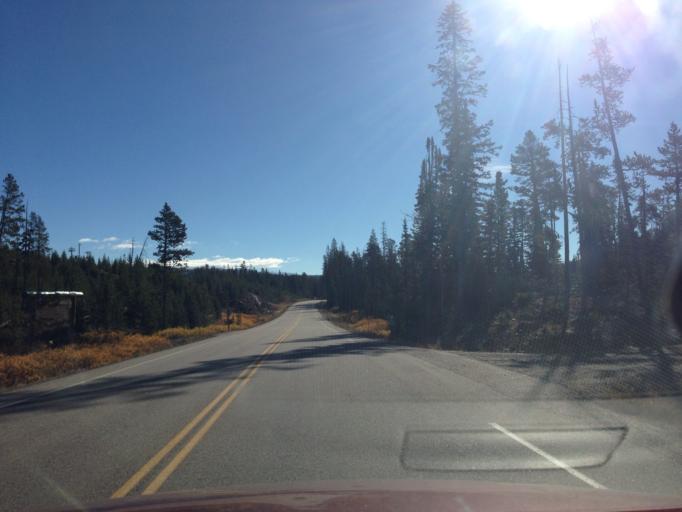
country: US
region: Montana
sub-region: Carbon County
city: Red Lodge
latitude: 45.0267
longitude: -109.8897
